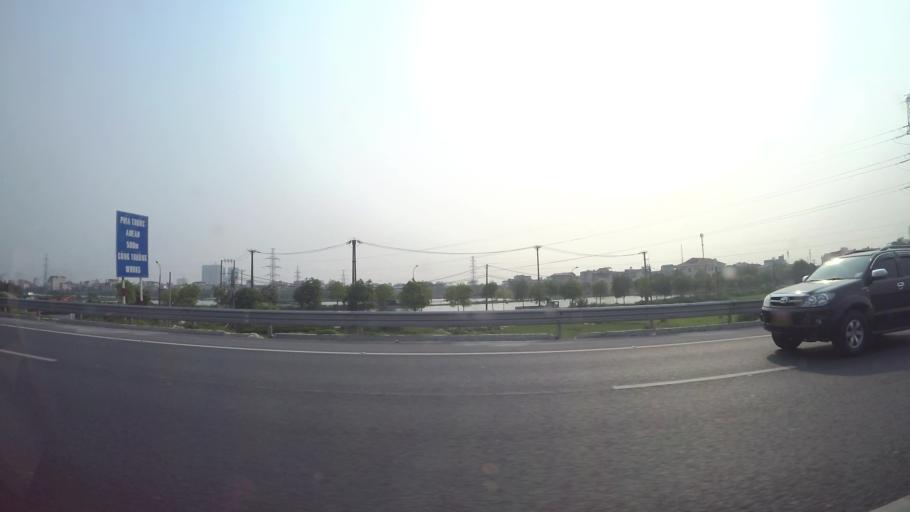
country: VN
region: Ha Noi
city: Van Dien
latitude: 20.9462
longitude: 105.8574
